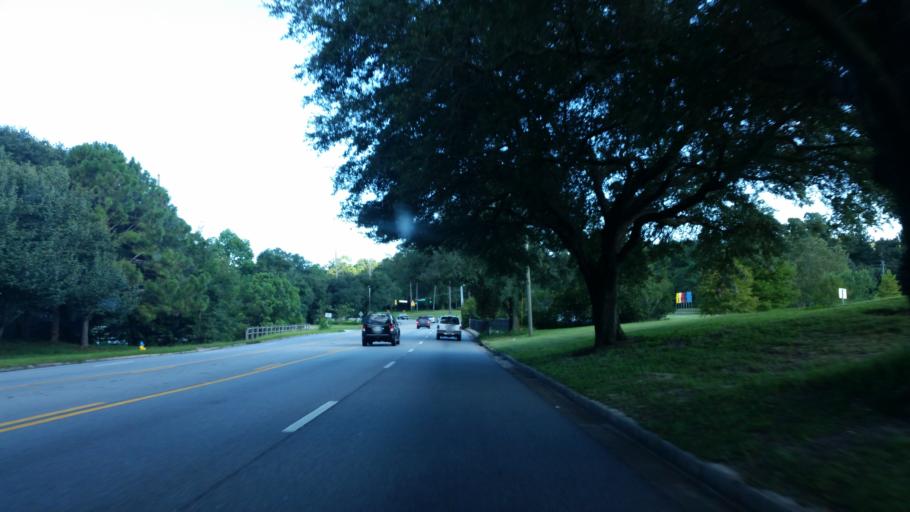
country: US
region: Alabama
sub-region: Mobile County
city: Prichard
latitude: 30.7069
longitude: -88.1519
